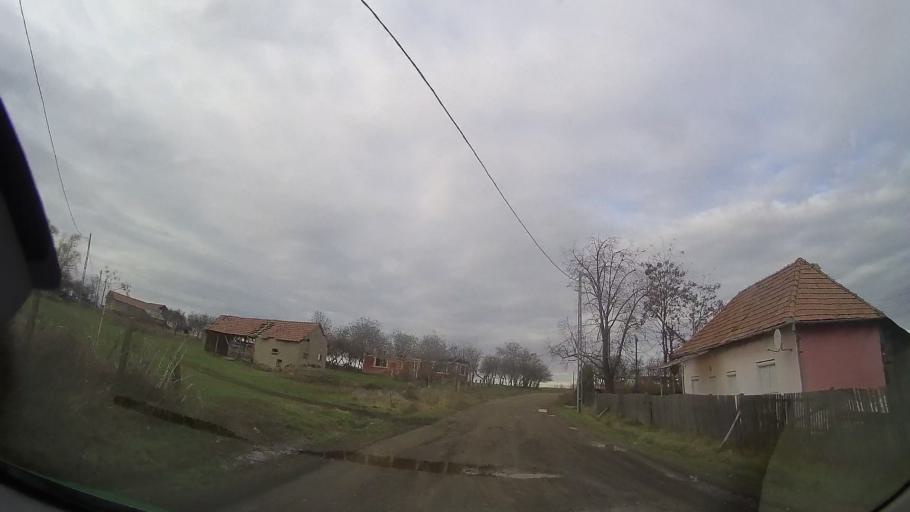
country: RO
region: Bistrita-Nasaud
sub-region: Comuna Milas
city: Milas
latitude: 46.8284
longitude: 24.4674
